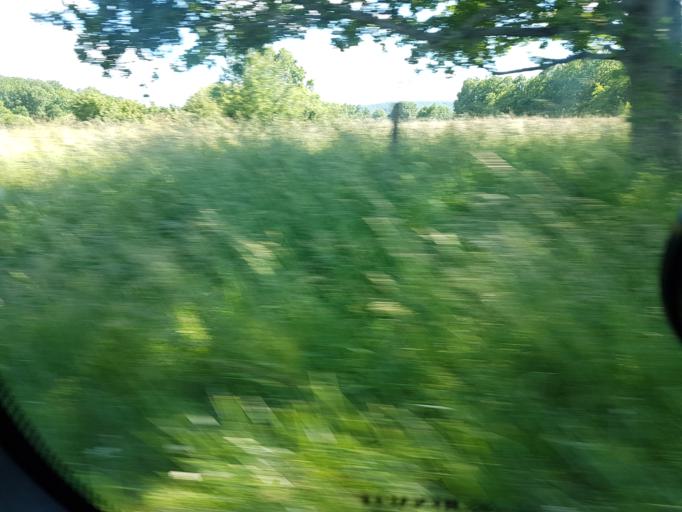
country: FR
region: Bourgogne
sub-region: Departement de Saone-et-Loire
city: Epinac
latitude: 46.9895
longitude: 4.4936
